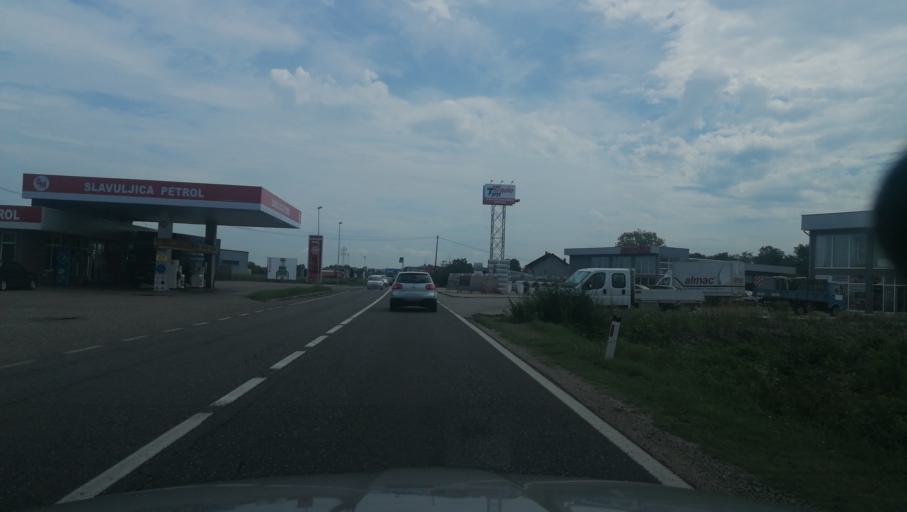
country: BA
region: Federation of Bosnia and Herzegovina
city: Odzak
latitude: 44.9660
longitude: 18.3107
